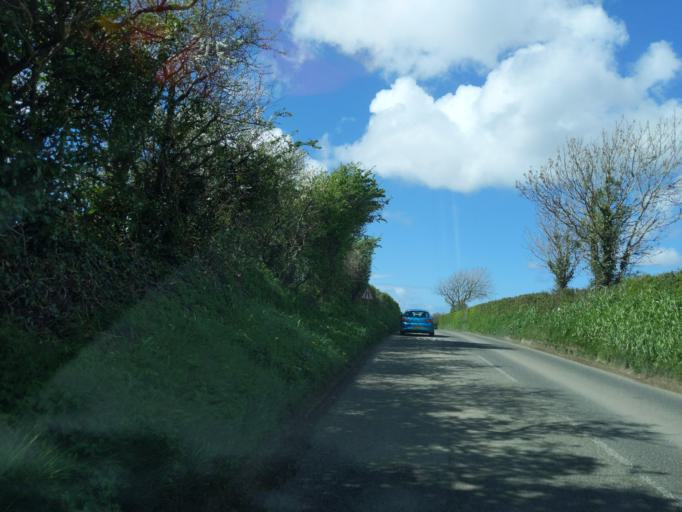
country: GB
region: England
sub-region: Cornwall
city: Wadebridge
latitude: 50.5296
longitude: -4.8351
